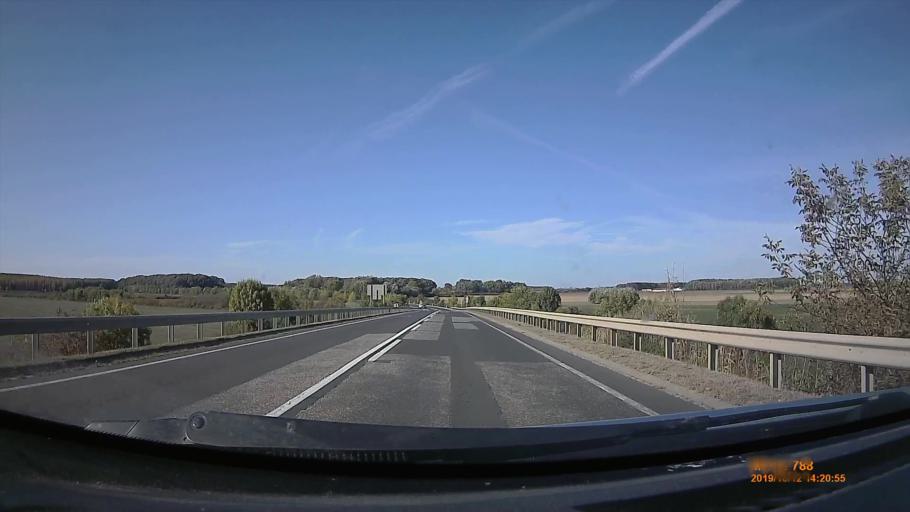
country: HU
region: Hajdu-Bihar
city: Biharkeresztes
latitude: 47.1345
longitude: 21.7407
